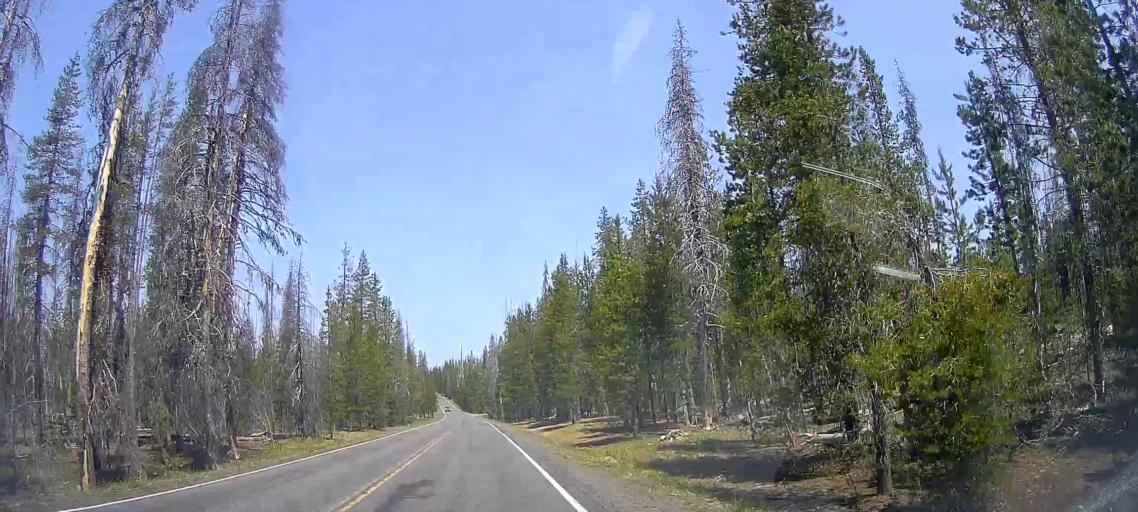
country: US
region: Oregon
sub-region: Lane County
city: Oakridge
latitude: 43.0452
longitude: -122.1186
